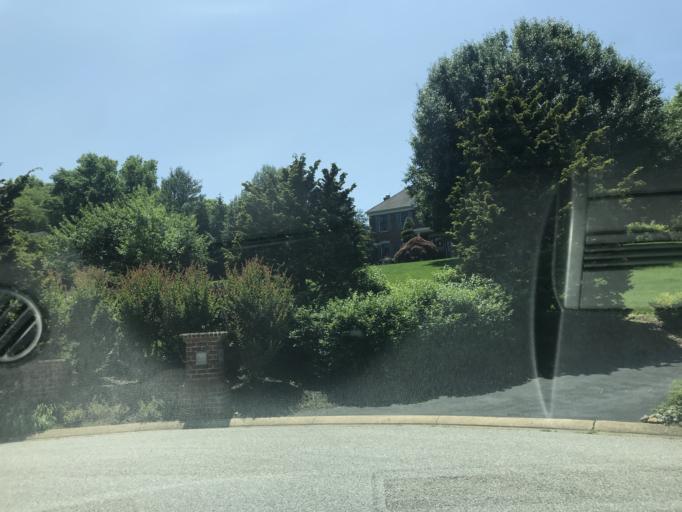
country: US
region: Maryland
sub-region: Harford County
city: South Bel Air
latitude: 39.5641
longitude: -76.2730
